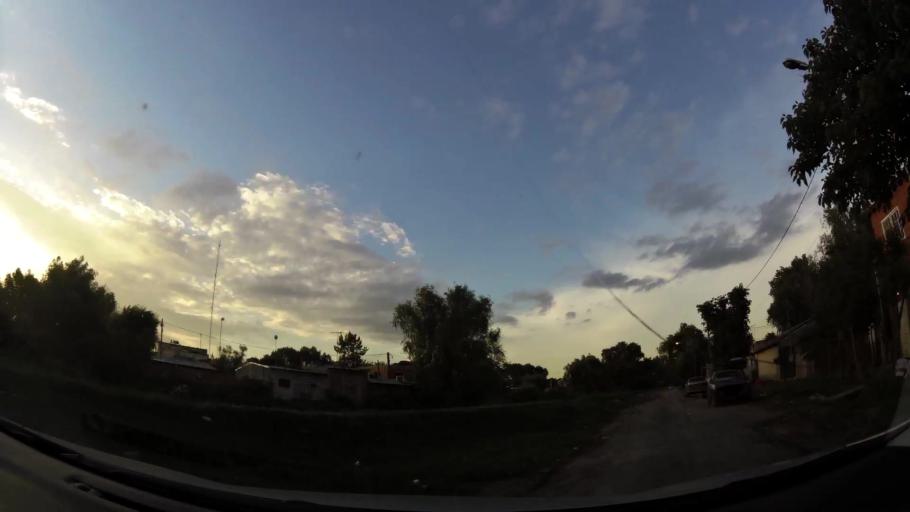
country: AR
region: Buenos Aires
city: Santa Catalina - Dique Lujan
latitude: -34.4479
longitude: -58.6665
